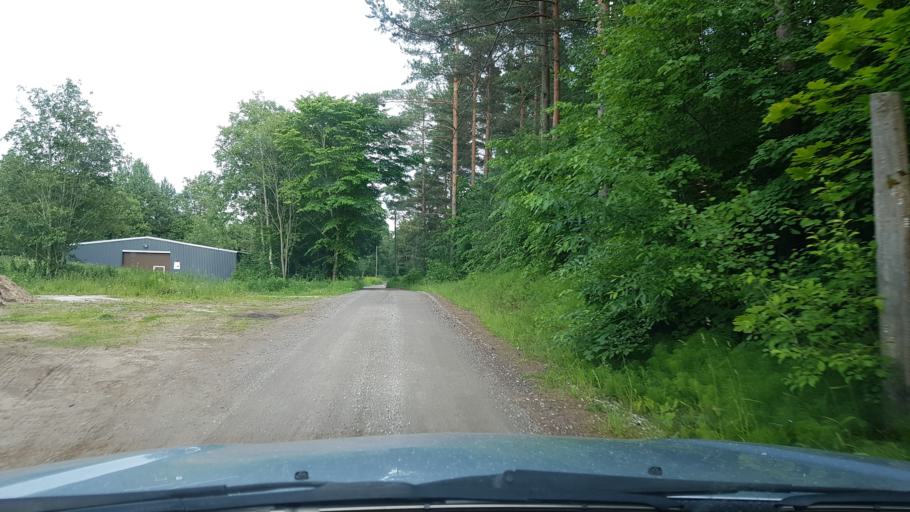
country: EE
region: Ida-Virumaa
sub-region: Narva-Joesuu linn
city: Narva-Joesuu
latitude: 59.4580
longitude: 28.0644
